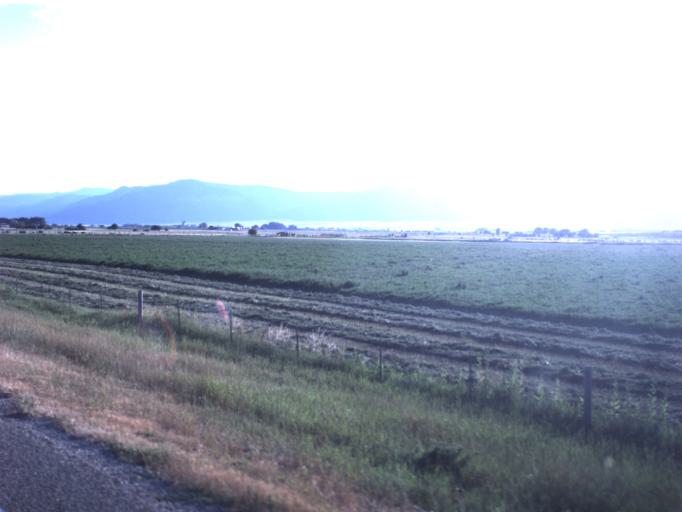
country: US
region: Utah
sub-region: Sanpete County
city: Mount Pleasant
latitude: 39.4988
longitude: -111.5063
